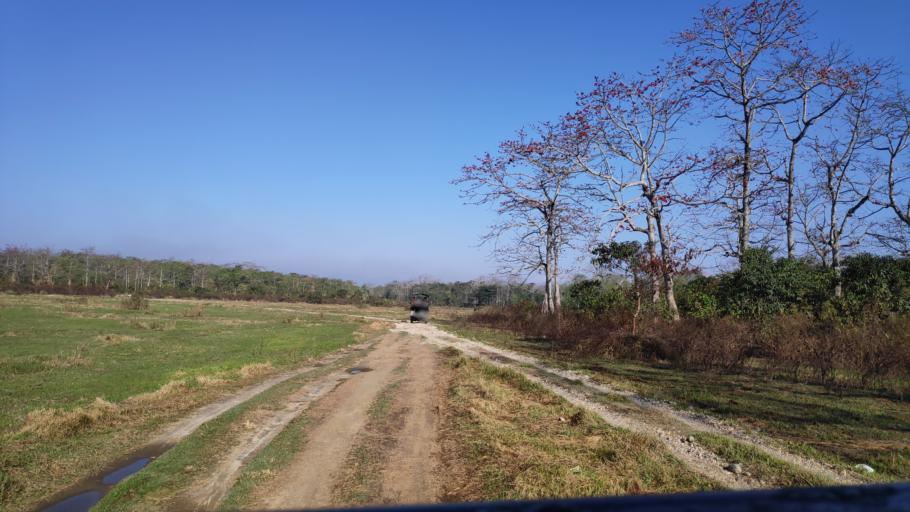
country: NP
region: Central Region
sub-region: Narayani Zone
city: Bharatpur
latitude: 27.5599
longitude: 84.5240
